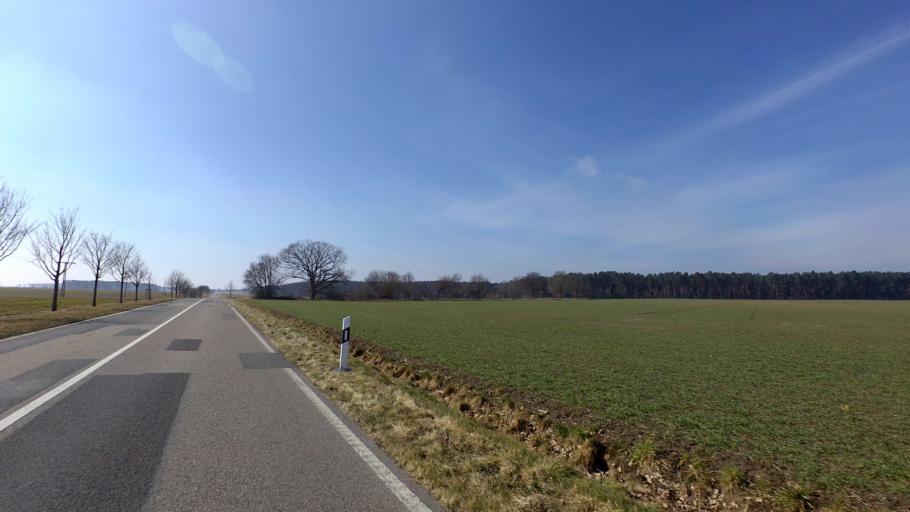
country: DE
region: Brandenburg
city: Wiesenburg
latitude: 52.0713
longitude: 12.5157
